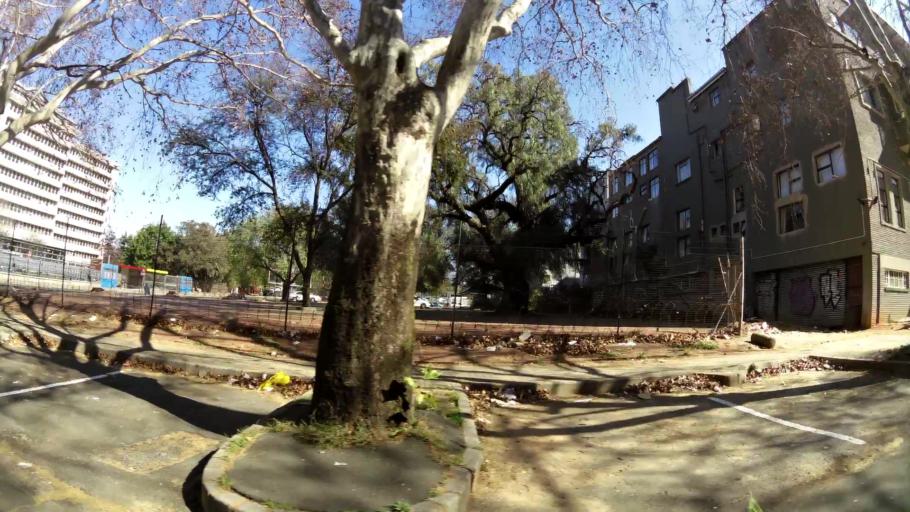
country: ZA
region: Gauteng
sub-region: City of Johannesburg Metropolitan Municipality
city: Johannesburg
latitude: -26.1939
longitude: 28.0300
